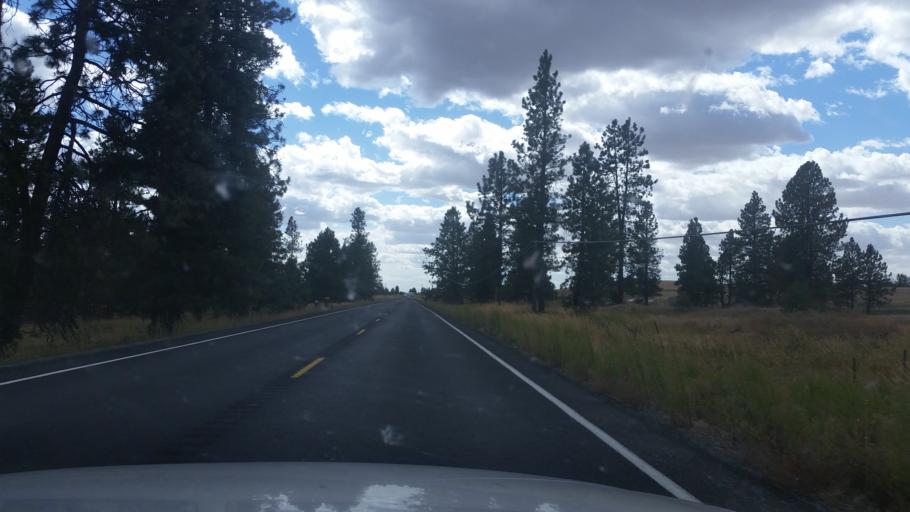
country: US
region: Washington
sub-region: Spokane County
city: Medical Lake
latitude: 47.5400
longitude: -117.7078
